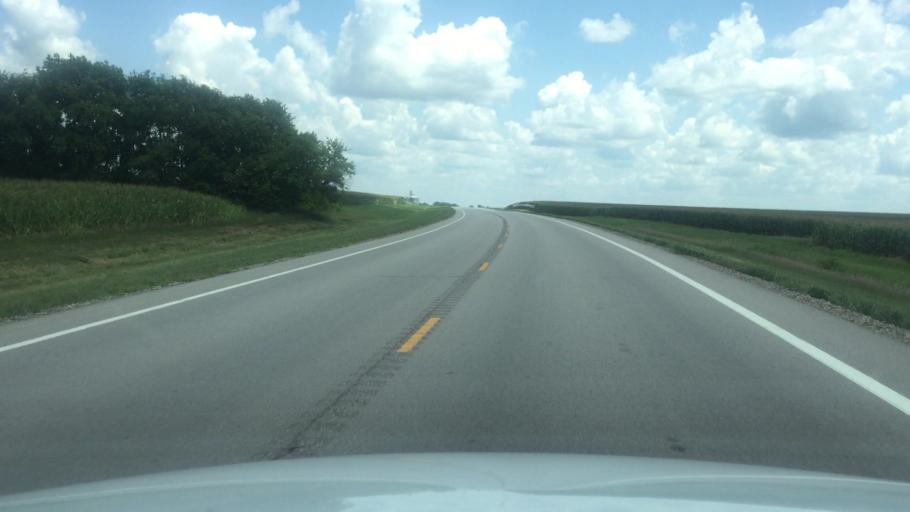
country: US
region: Kansas
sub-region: Brown County
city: Horton
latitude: 39.6604
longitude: -95.4062
